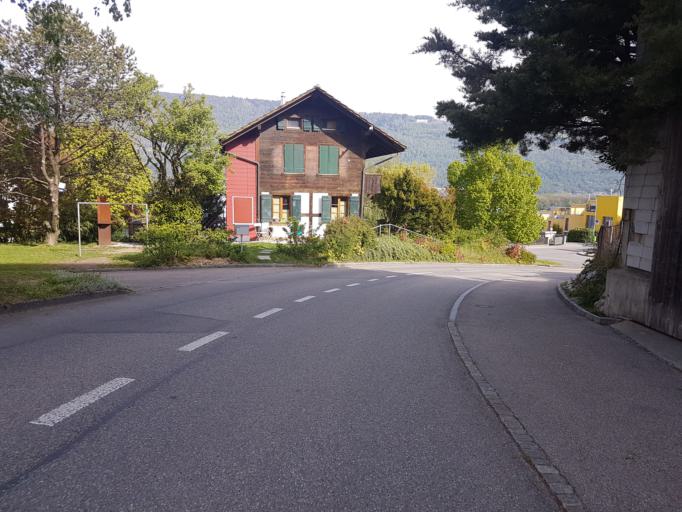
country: CH
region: Bern
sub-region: Biel/Bienne District
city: Bellmund
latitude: 47.1126
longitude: 7.2341
